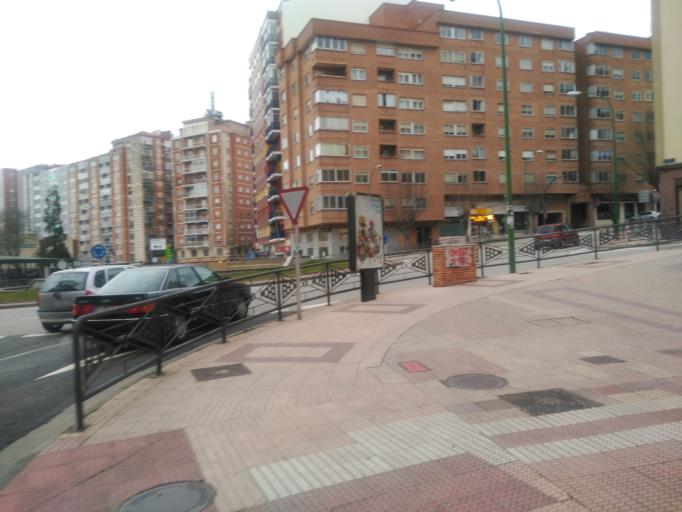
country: ES
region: Castille and Leon
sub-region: Provincia de Burgos
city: Burgos
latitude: 42.3328
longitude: -3.6999
